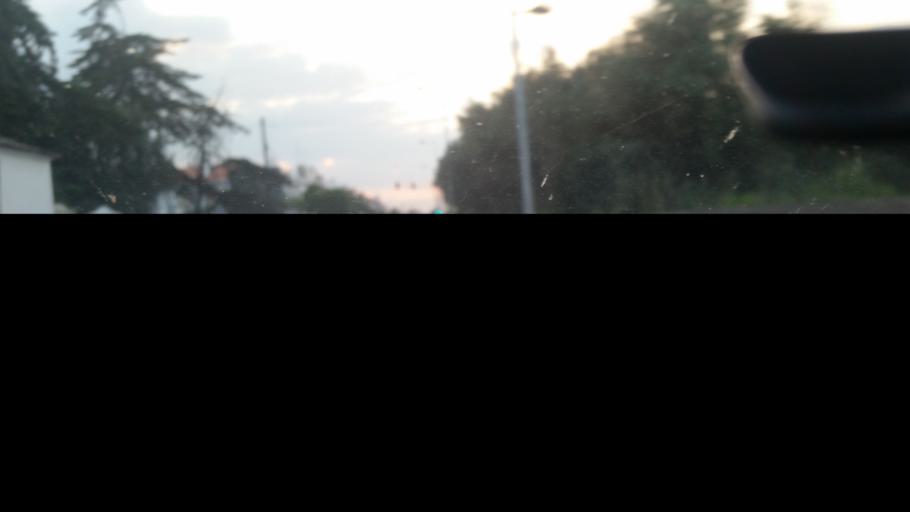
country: PT
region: Evora
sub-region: Evora
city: Evora
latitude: 38.5763
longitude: -7.9156
